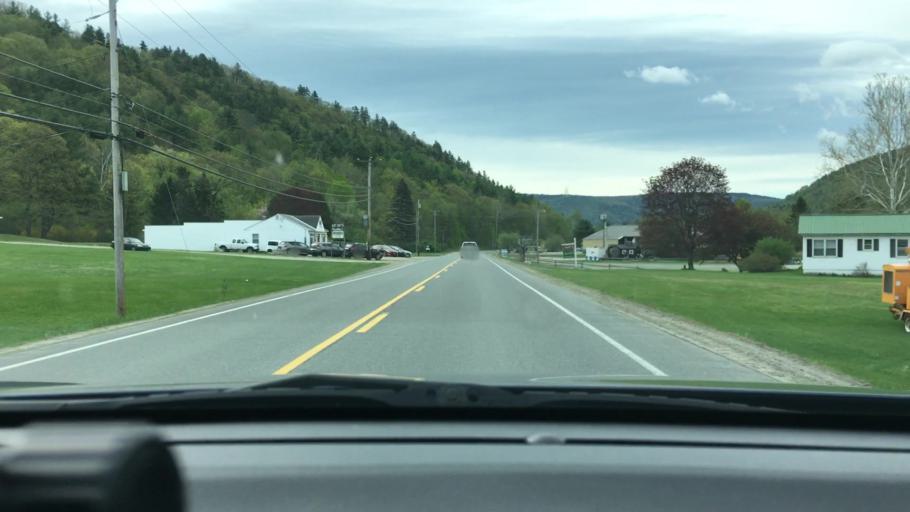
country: US
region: Vermont
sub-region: Windham County
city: Newfane
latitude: 43.0299
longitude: -72.6597
